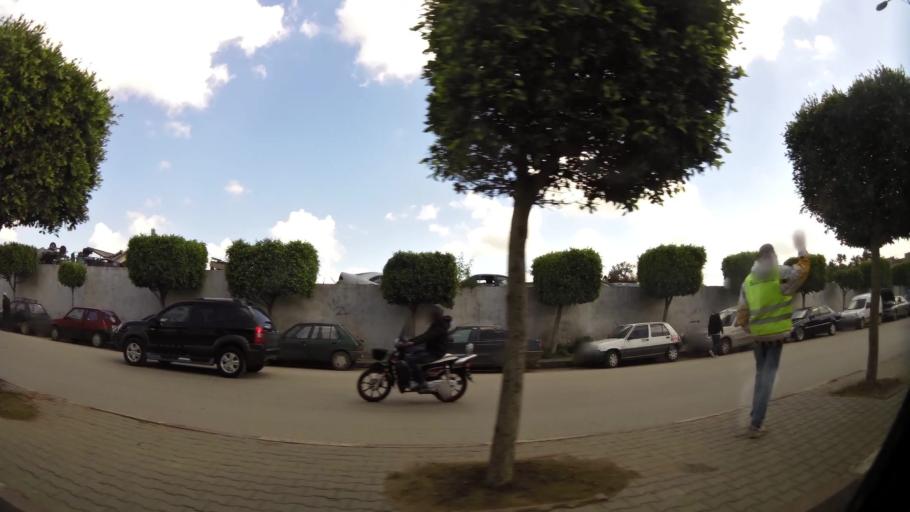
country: MA
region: Grand Casablanca
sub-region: Casablanca
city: Casablanca
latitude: 33.5402
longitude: -7.5579
